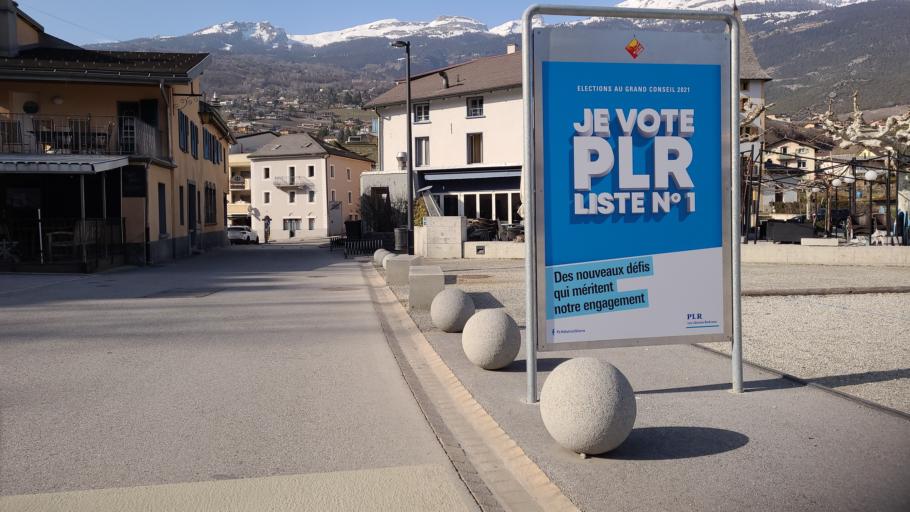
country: CH
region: Valais
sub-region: Sierre District
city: Sierre
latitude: 46.2964
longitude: 7.5428
